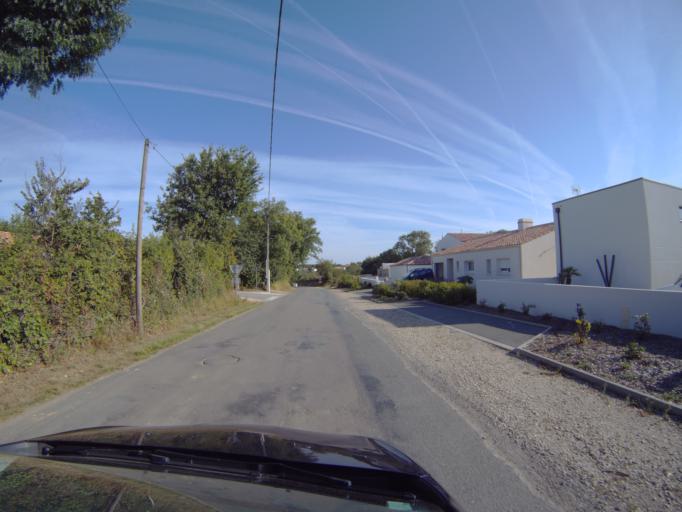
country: FR
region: Pays de la Loire
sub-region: Departement de la Vendee
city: Saint-Hilaire-de-Talmont
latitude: 46.4661
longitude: -1.6044
